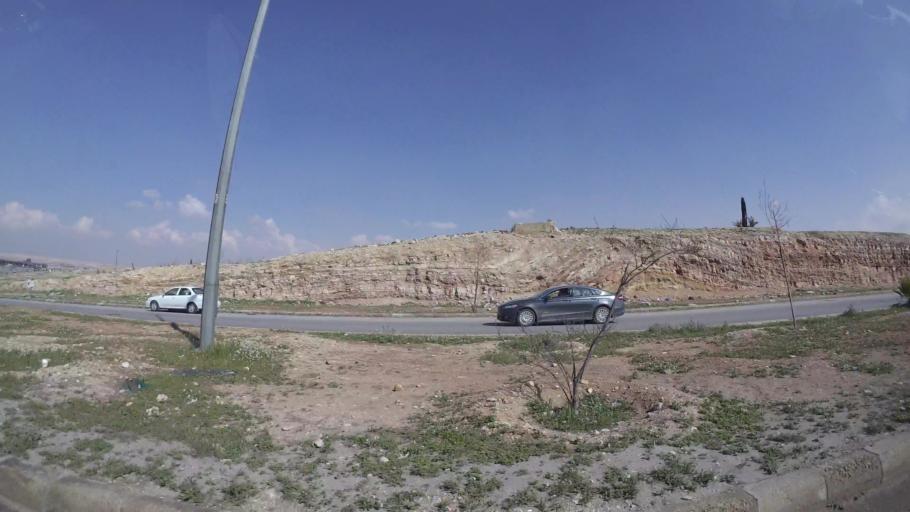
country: JO
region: Zarqa
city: Zarqa
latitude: 32.0742
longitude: 36.1036
